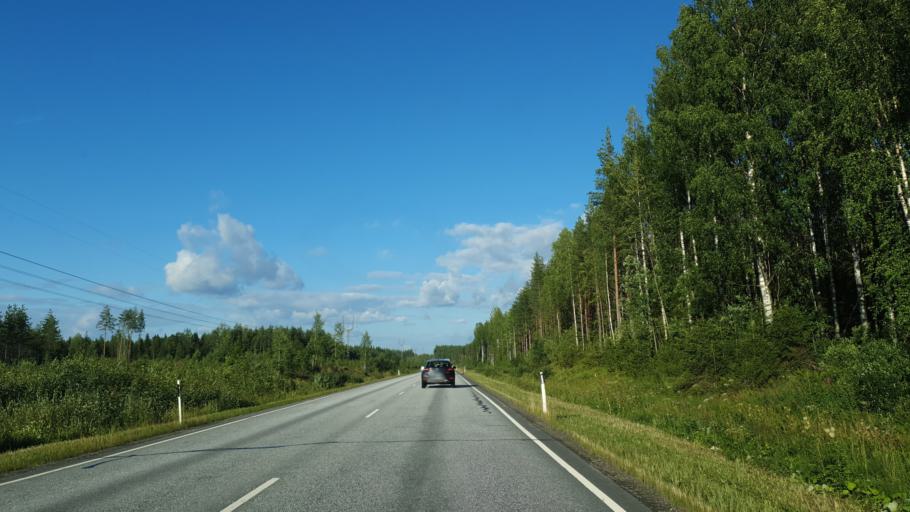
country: FI
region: North Karelia
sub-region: Joensuu
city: Outokumpu
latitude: 62.5325
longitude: 29.0948
